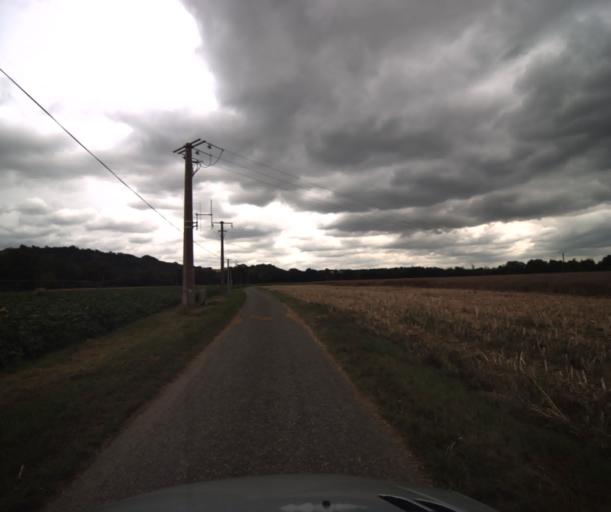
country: FR
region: Midi-Pyrenees
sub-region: Departement de la Haute-Garonne
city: Labarthe-sur-Leze
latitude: 43.4646
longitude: 1.4133
